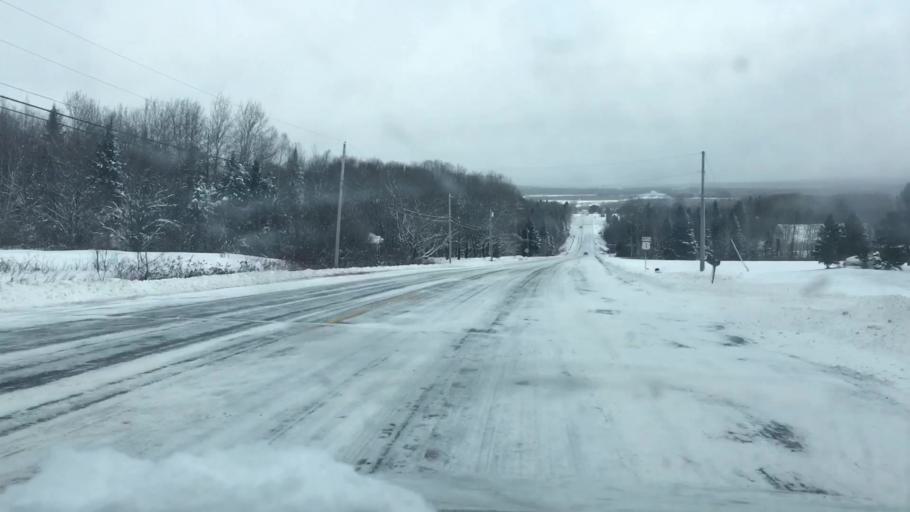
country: US
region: Maine
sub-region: Aroostook County
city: Van Buren
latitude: 47.1402
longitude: -67.9499
